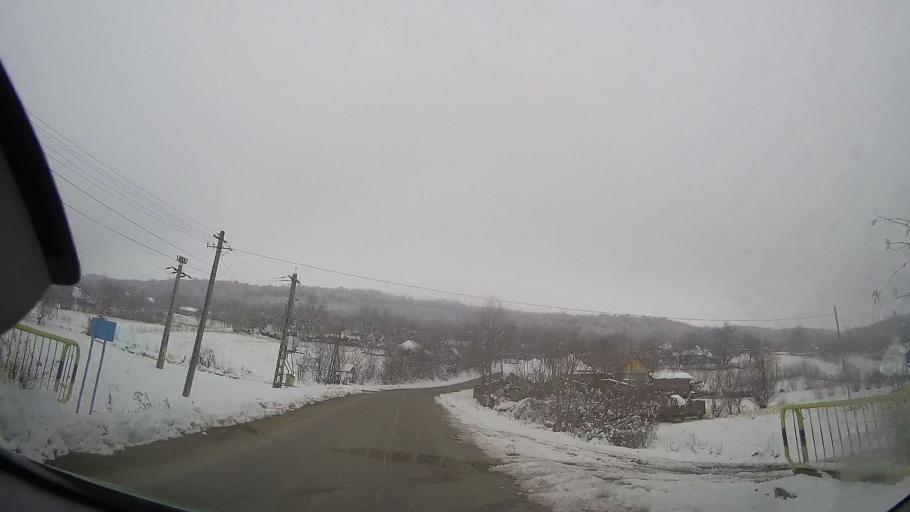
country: RO
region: Neamt
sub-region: Comuna Bozieni
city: Bozieni
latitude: 46.8525
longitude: 27.1798
